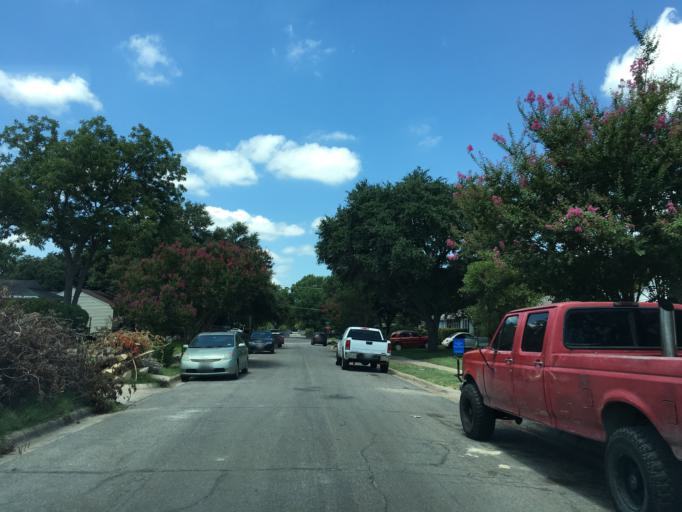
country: US
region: Texas
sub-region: Dallas County
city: Garland
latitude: 32.8419
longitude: -96.6720
